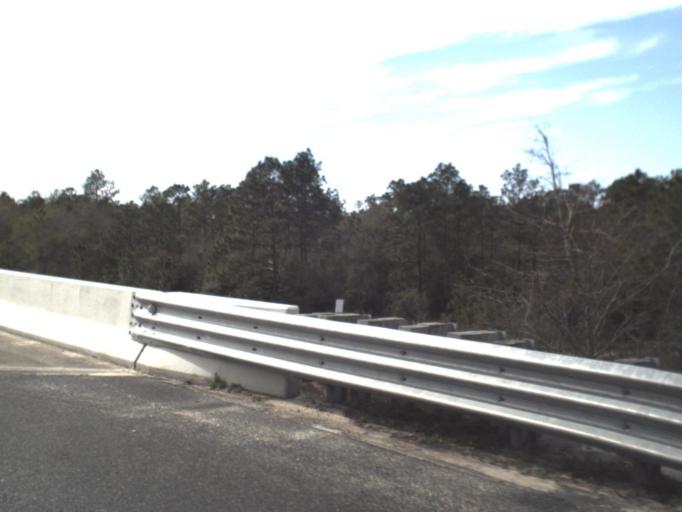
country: US
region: Florida
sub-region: Bay County
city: Youngstown
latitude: 30.5290
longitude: -85.3999
